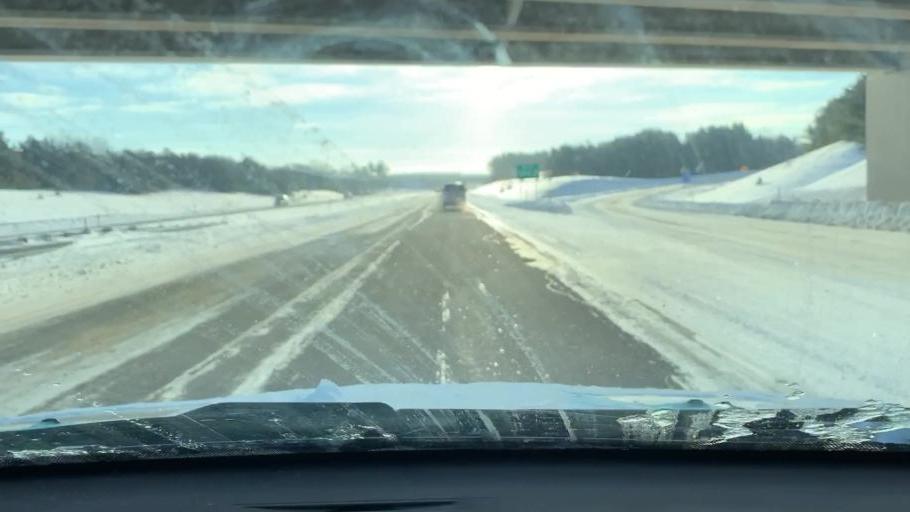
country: US
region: Michigan
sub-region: Wexford County
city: Cadillac
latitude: 44.2574
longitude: -85.3786
